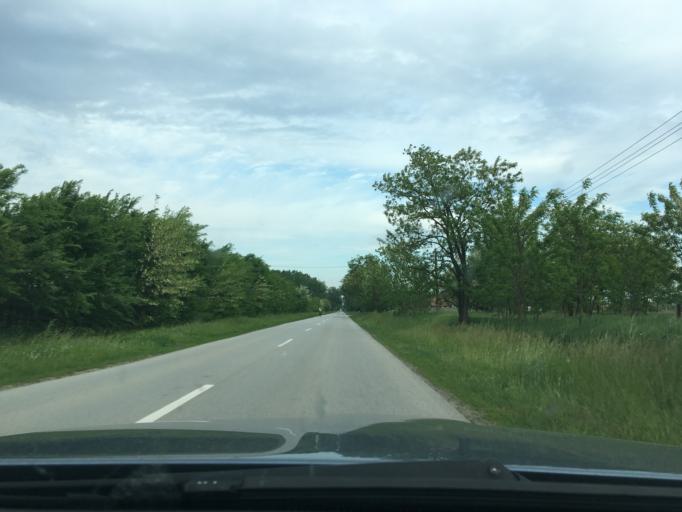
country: HU
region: Hajdu-Bihar
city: Debrecen
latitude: 47.5494
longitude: 21.6794
